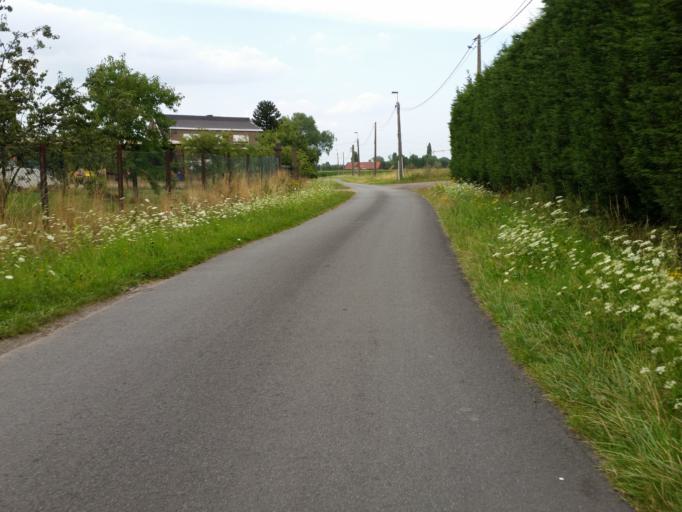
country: BE
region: Flanders
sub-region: Provincie Antwerpen
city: Rumst
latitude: 51.1016
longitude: 4.4362
